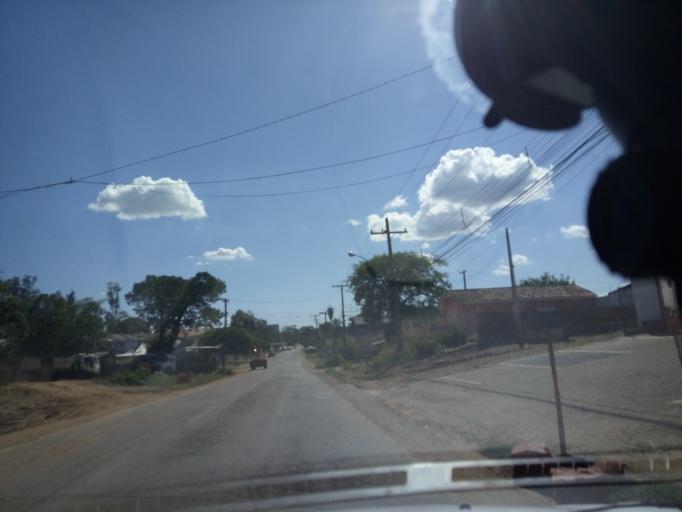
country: BR
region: Rio Grande do Sul
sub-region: Santa Maria
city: Santa Maria
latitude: -29.6980
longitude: -53.7246
